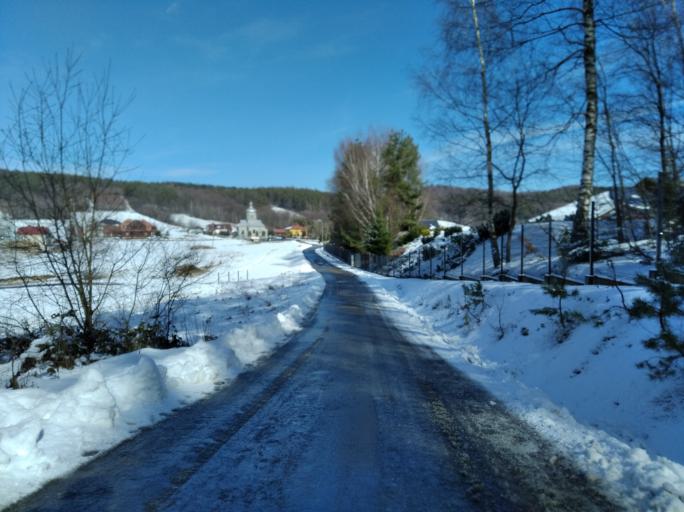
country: PL
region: Subcarpathian Voivodeship
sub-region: Powiat krosnienski
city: Korczyna
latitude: 49.7446
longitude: 21.8176
